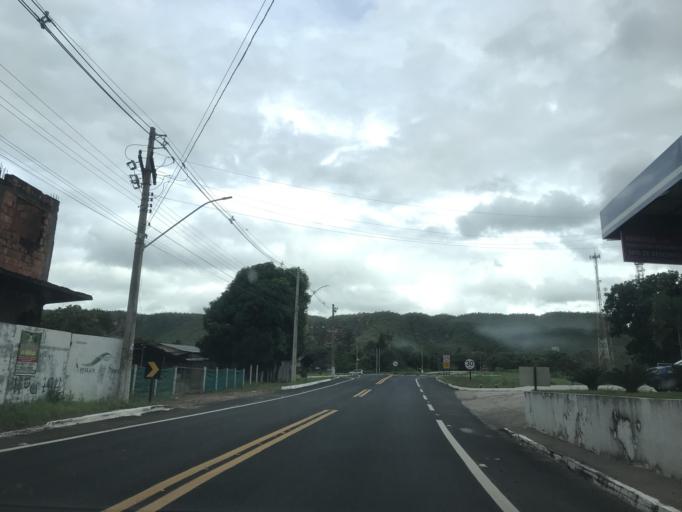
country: BR
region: Goias
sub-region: Caldas Novas
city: Caldas Novas
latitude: -17.7660
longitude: -48.7580
